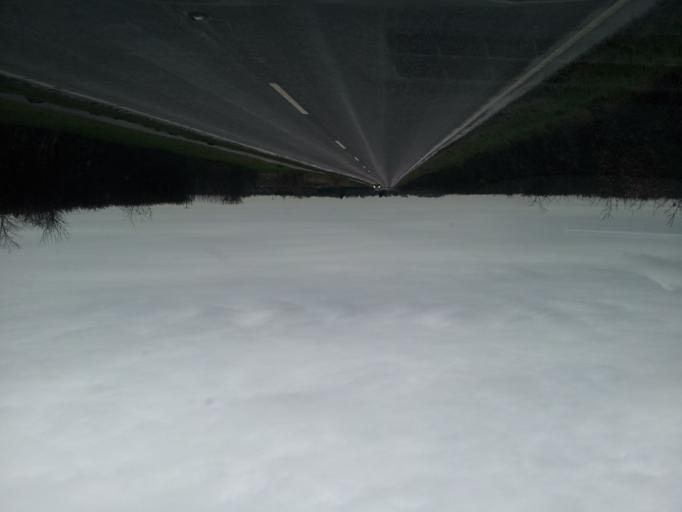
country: GB
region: England
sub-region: Cambridgeshire
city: Bottisham
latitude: 52.2396
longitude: 0.2601
